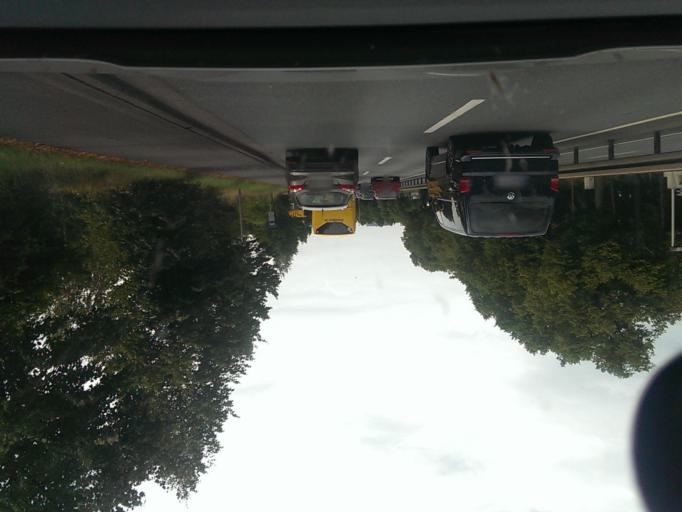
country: DE
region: Lower Saxony
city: Auf der Horst
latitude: 52.4097
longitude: 9.6524
